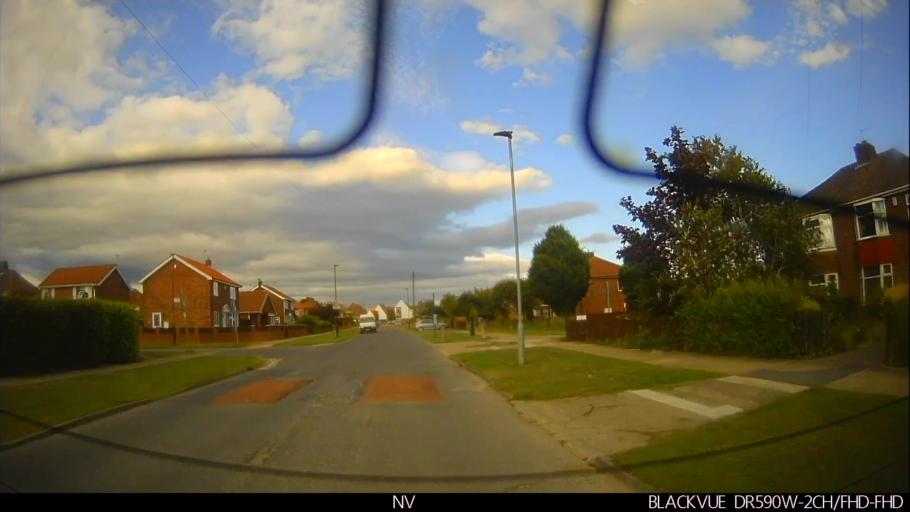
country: GB
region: England
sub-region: City of York
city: Heslington
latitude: 53.9605
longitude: -1.0501
